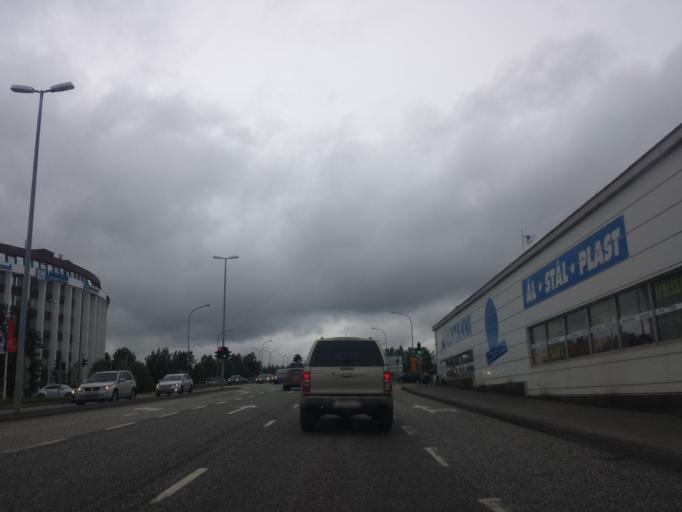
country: IS
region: Capital Region
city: Reykjavik
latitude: 64.1263
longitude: -21.8122
